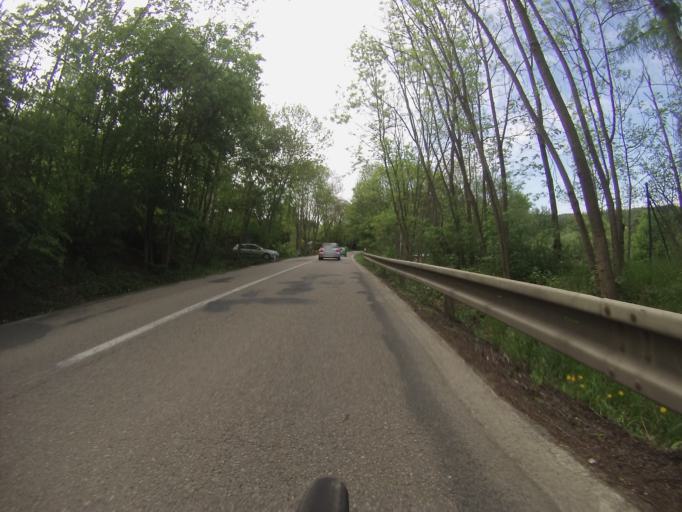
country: CZ
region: South Moravian
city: Kurim
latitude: 49.2437
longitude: 16.4977
